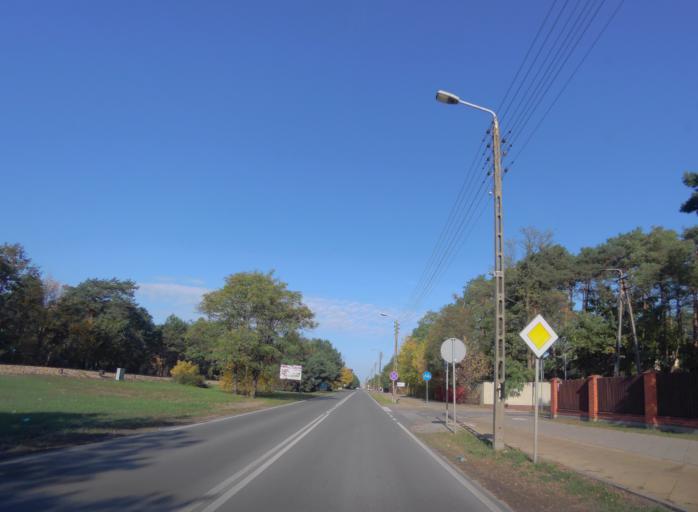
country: PL
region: Masovian Voivodeship
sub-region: Powiat otwocki
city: Jozefow
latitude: 52.1421
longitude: 21.2312
